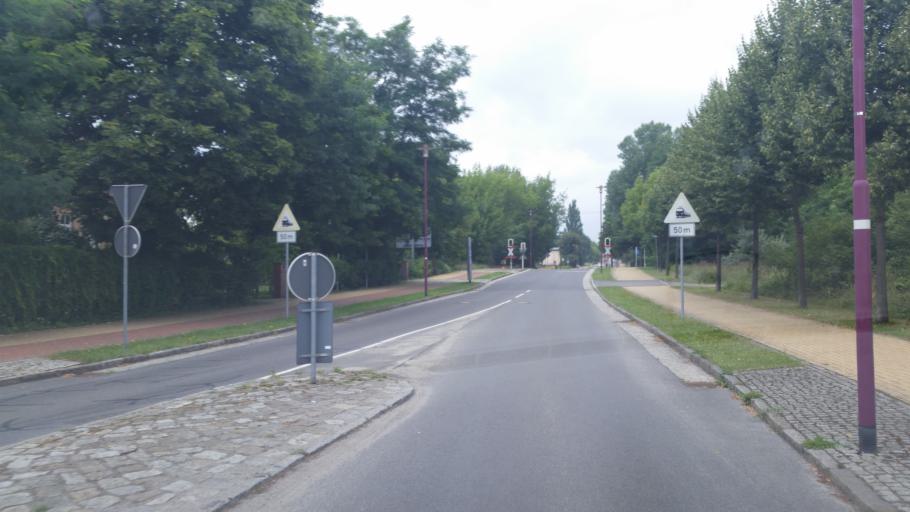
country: DE
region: Brandenburg
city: Grossraschen
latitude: 51.5783
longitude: 14.0102
